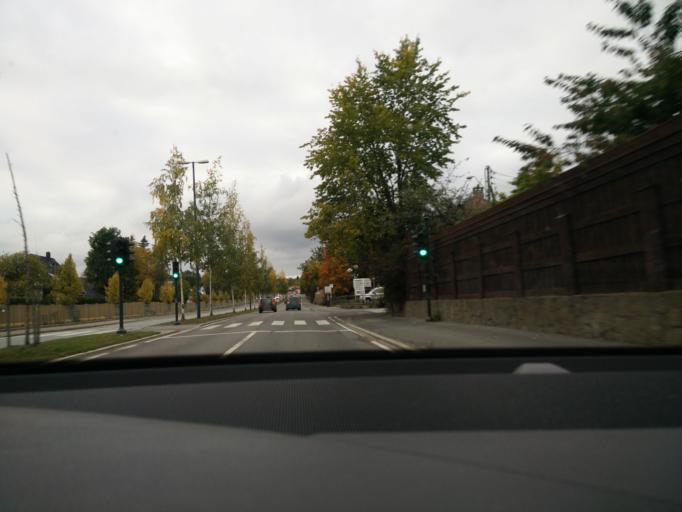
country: NO
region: Oslo
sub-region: Oslo
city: Sjolyststranda
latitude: 59.9357
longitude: 10.6916
